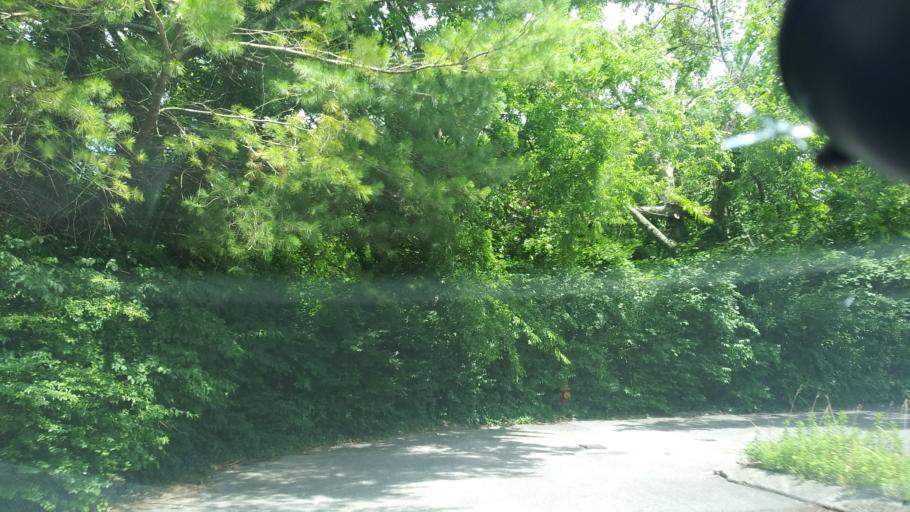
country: US
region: Tennessee
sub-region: Davidson County
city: Belle Meade
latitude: 36.1401
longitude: -86.8328
